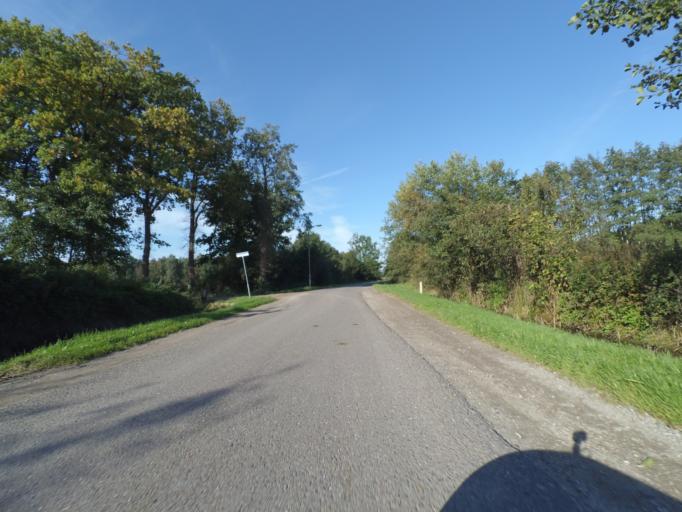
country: NL
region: Gelderland
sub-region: Gemeente Nijkerk
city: Nijkerk
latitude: 52.2245
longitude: 5.5168
